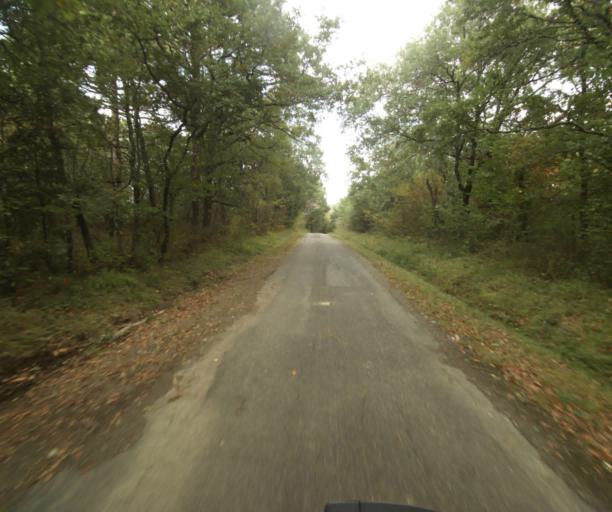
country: FR
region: Midi-Pyrenees
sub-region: Departement de la Haute-Garonne
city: Launac
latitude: 43.8301
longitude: 1.1151
